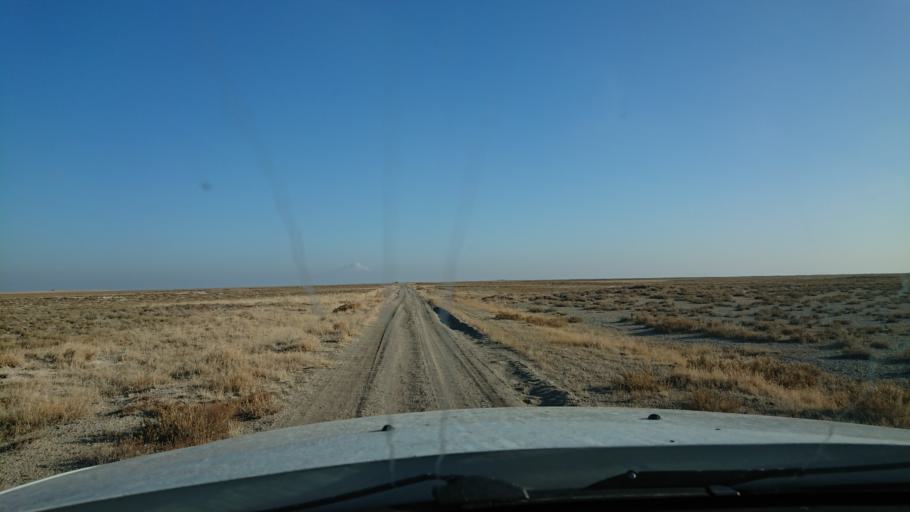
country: TR
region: Aksaray
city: Sultanhani
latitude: 38.4035
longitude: 33.5761
